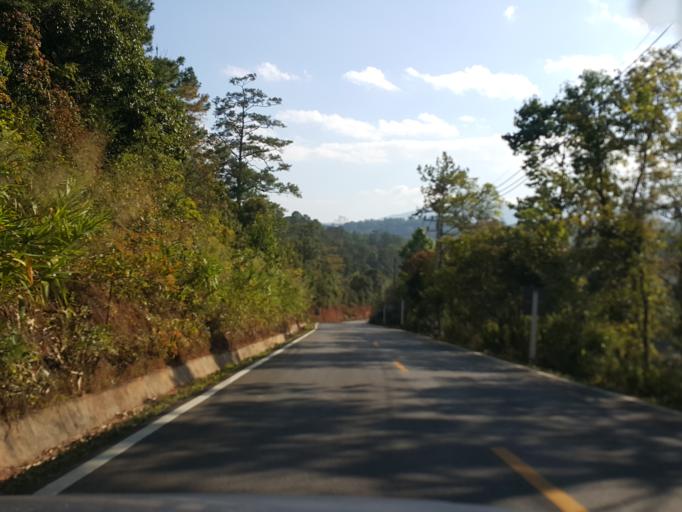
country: TH
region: Chiang Mai
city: Mae Wang
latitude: 18.6686
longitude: 98.5505
